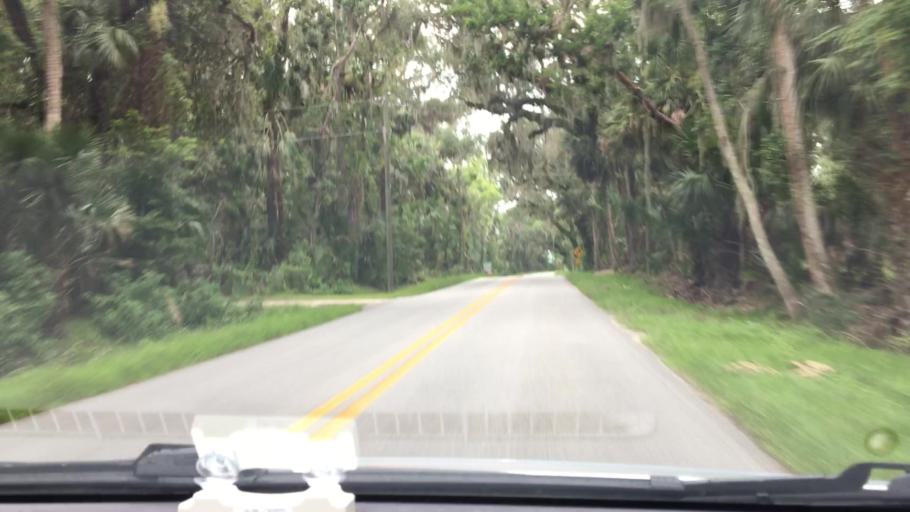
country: US
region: Florida
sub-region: Volusia County
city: Deltona
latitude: 28.8601
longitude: -81.2465
